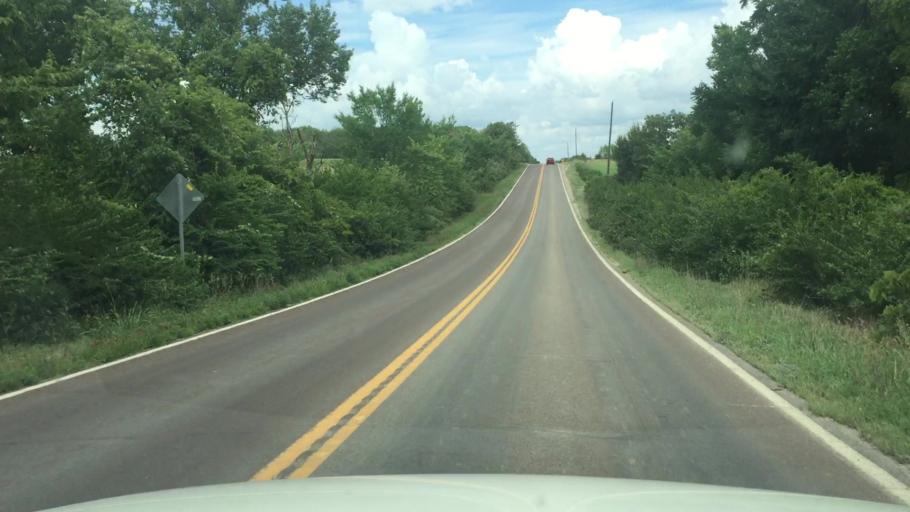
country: US
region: Kansas
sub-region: Shawnee County
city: Topeka
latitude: 39.0225
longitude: -95.5013
